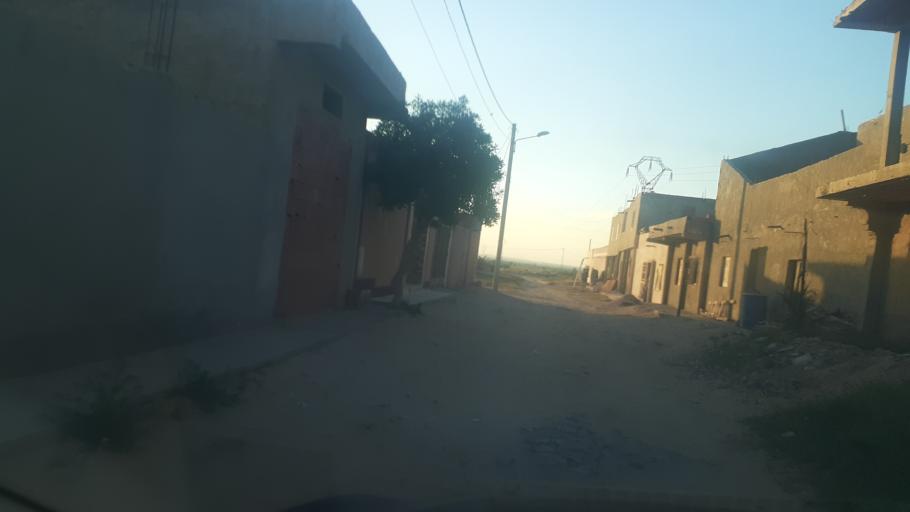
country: TN
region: Qabis
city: Gabes
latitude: 33.9323
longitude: 10.0387
